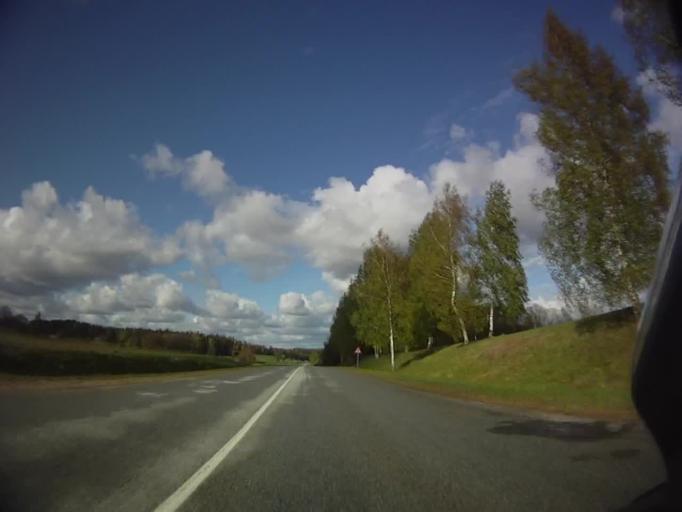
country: LV
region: Sigulda
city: Sigulda
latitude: 57.1711
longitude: 24.8145
